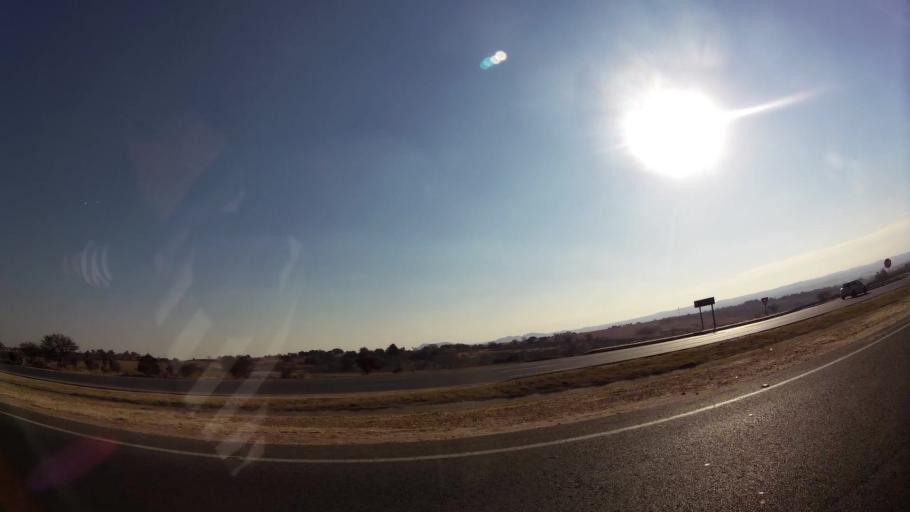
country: ZA
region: Gauteng
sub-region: West Rand District Municipality
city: Muldersdriseloop
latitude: -25.9853
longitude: 27.9251
